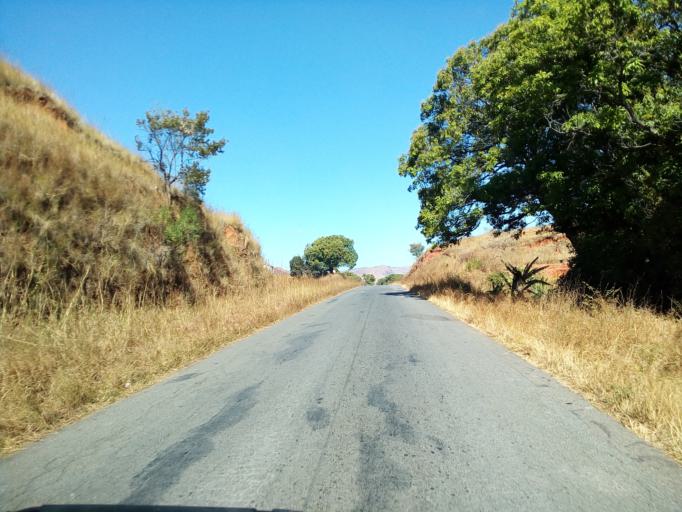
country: MG
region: Betsiboka
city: Maevatanana
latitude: -17.4673
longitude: 46.9897
